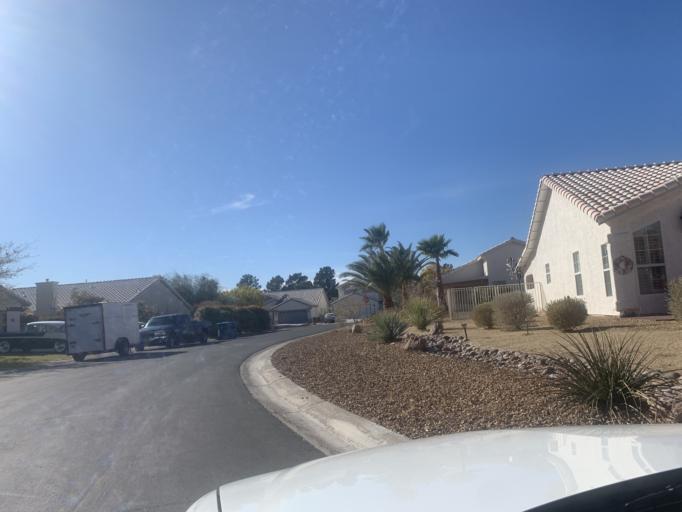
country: US
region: Nevada
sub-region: Clark County
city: Las Vegas
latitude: 36.2578
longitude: -115.2187
